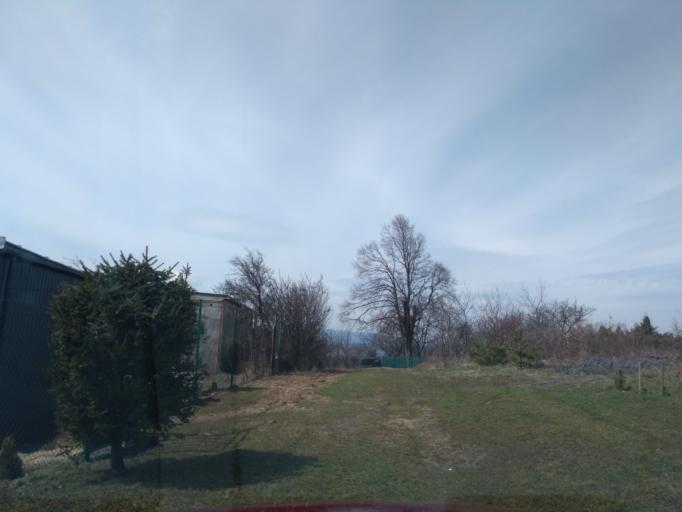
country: SK
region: Kosicky
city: Kosice
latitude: 48.7091
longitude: 21.2895
